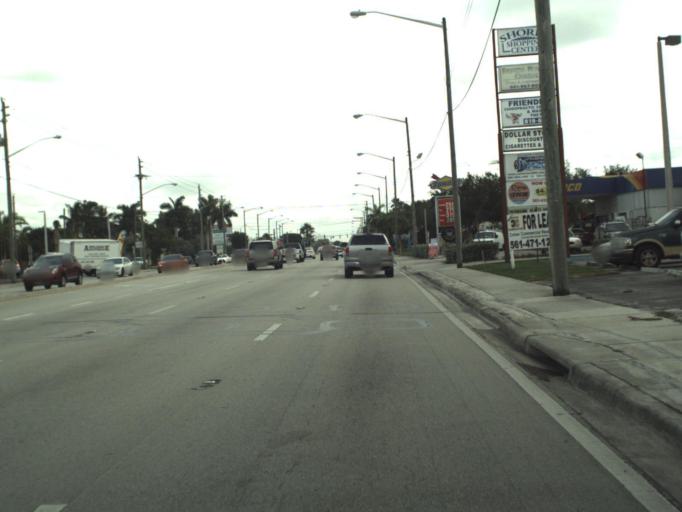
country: US
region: Florida
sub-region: Palm Beach County
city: Lake Clarke Shores
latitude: 26.6471
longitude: -80.0879
